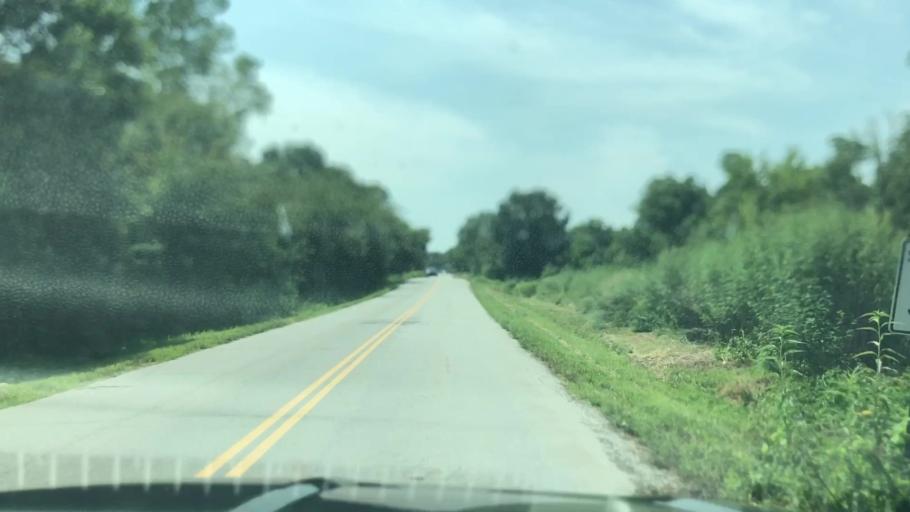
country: US
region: Oklahoma
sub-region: Ottawa County
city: Commerce
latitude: 36.9291
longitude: -94.8568
